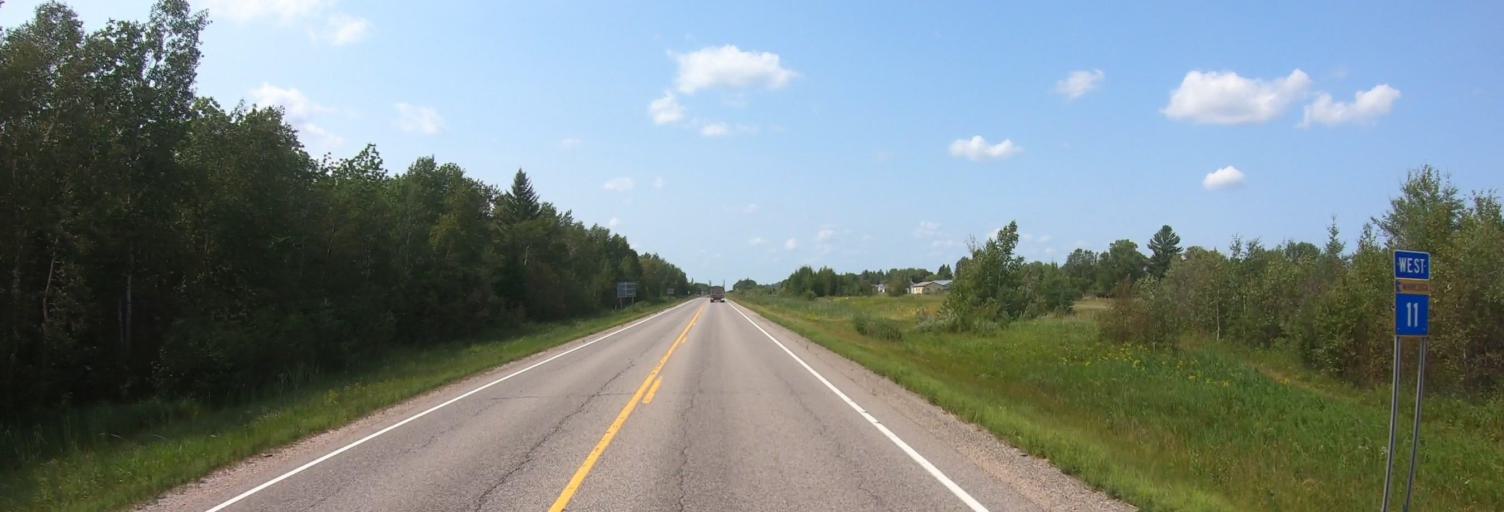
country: US
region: Minnesota
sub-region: Roseau County
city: Warroad
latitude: 48.7997
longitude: -95.0919
